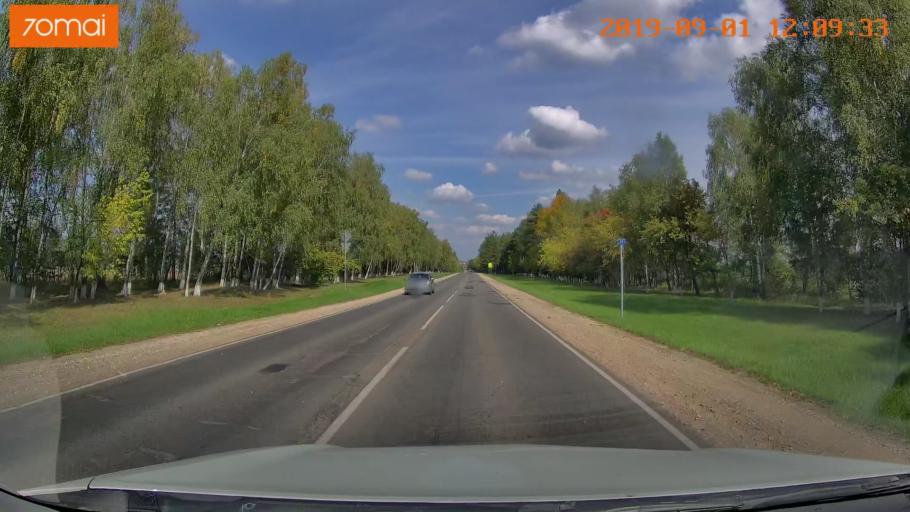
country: RU
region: Kaluga
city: Maloyaroslavets
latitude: 54.9817
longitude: 36.4267
